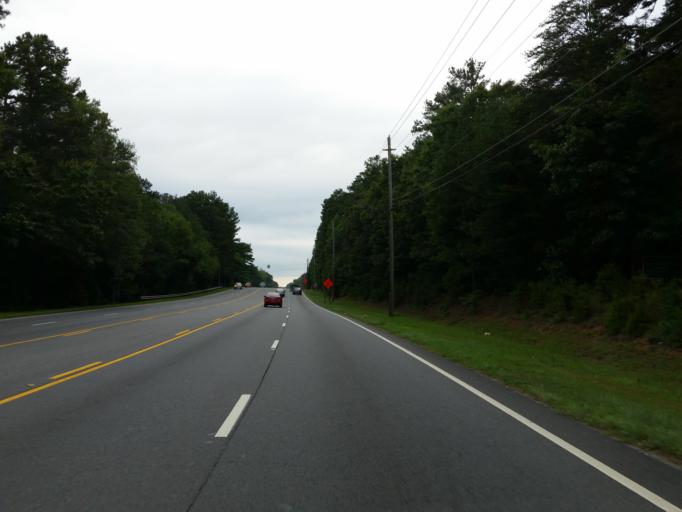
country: US
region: Georgia
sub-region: Cobb County
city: Fair Oaks
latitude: 33.9150
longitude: -84.5905
